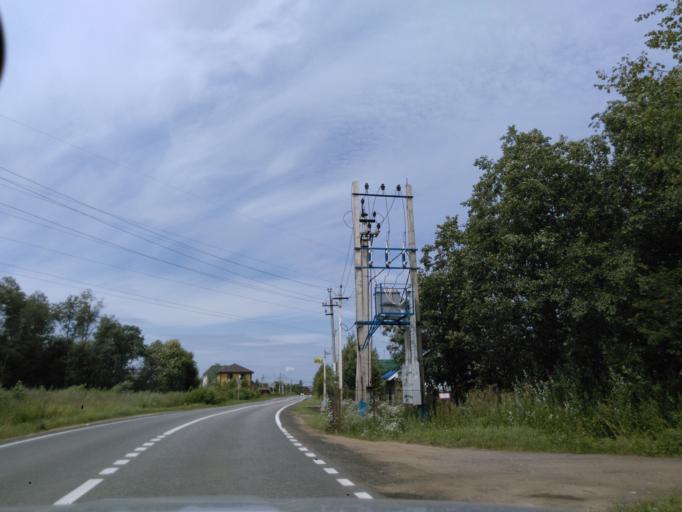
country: RU
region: Moskovskaya
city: Solnechnogorsk
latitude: 56.1568
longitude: 36.9815
